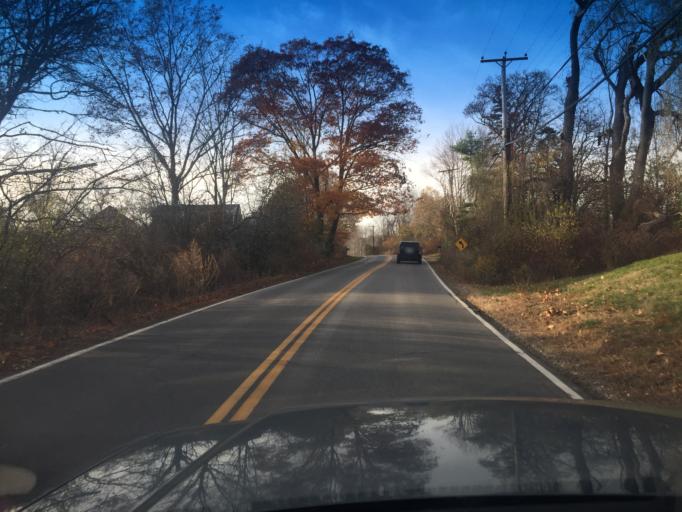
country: US
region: Maine
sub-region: York County
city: Eliot
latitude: 43.1784
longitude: -70.7275
